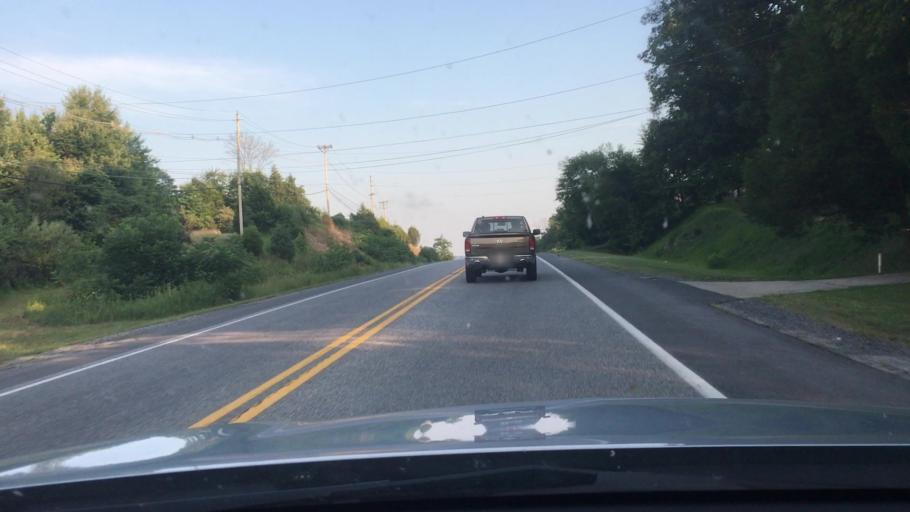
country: US
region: Pennsylvania
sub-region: York County
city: Dover
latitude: 40.0730
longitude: -76.9244
